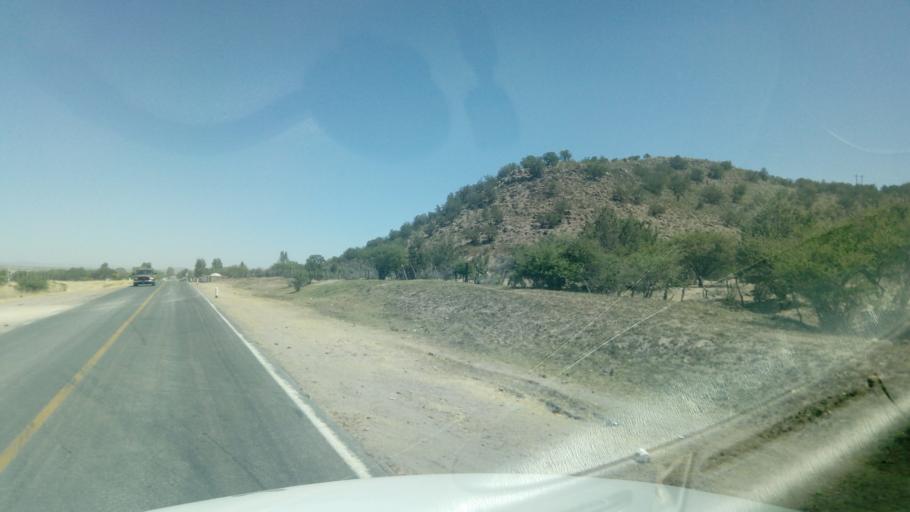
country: MX
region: Durango
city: Victoria de Durango
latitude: 24.1625
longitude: -104.7035
